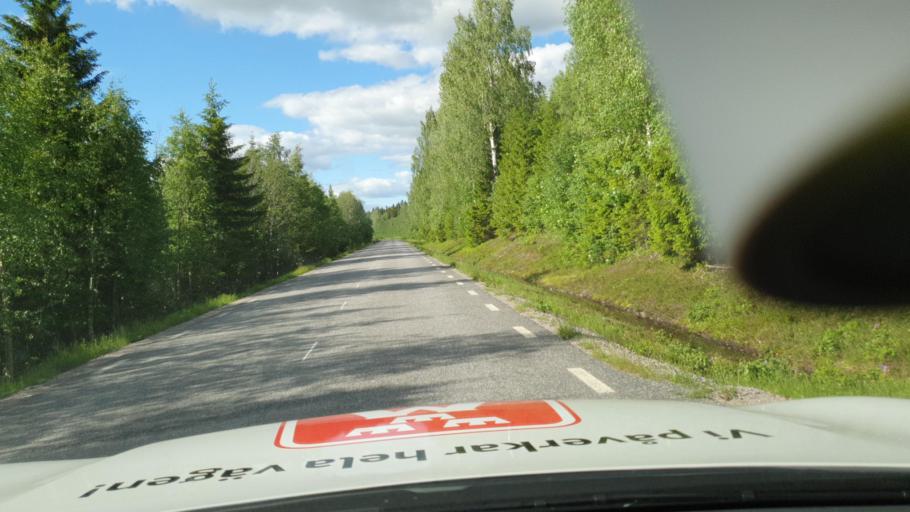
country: SE
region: Vaesterbotten
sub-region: Vannas Kommun
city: Vannasby
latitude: 63.8255
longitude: 19.8568
